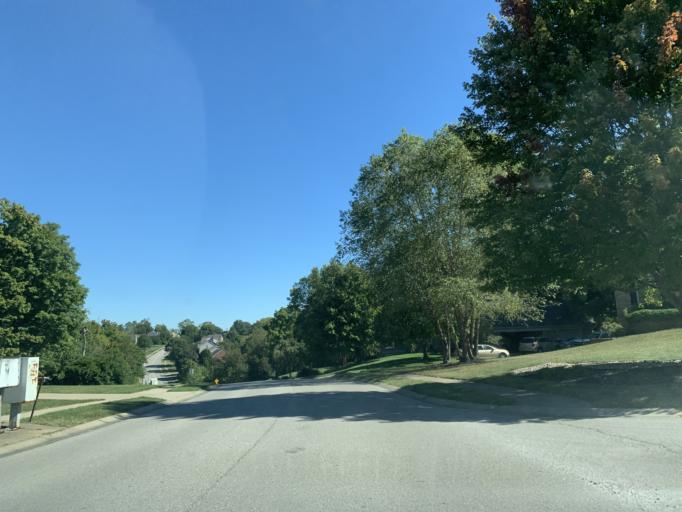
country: US
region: Kentucky
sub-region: Boone County
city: Francisville
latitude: 39.0993
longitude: -84.7274
